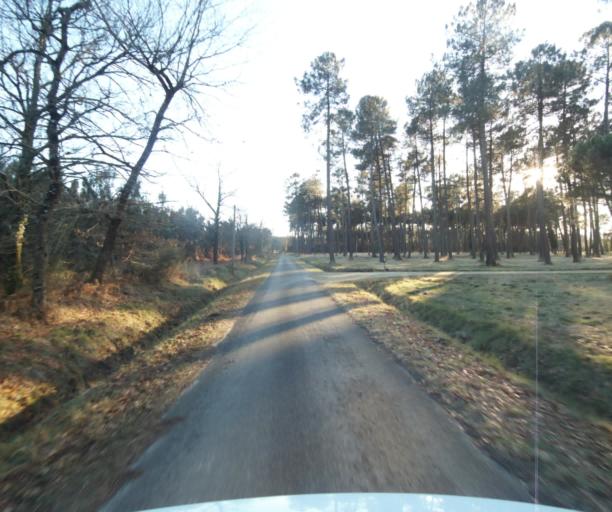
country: FR
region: Aquitaine
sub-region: Departement des Landes
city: Gabarret
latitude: 44.1043
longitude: -0.0799
